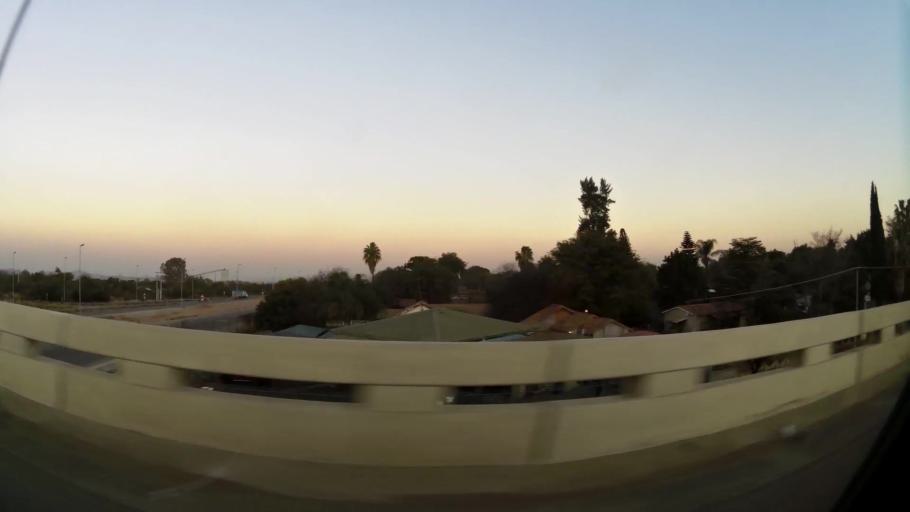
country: ZA
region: North-West
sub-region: Bojanala Platinum District Municipality
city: Rustenburg
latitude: -25.6477
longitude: 27.2551
